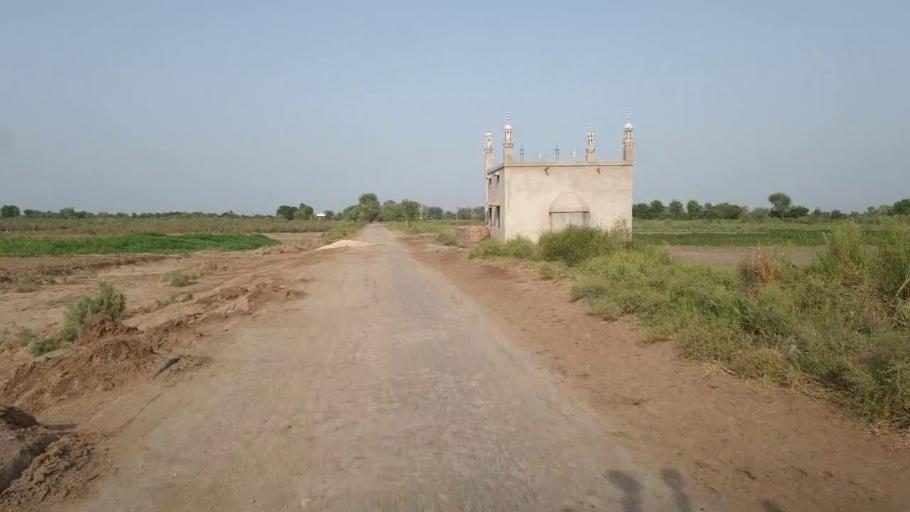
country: PK
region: Sindh
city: Daur
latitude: 26.3399
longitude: 68.2464
